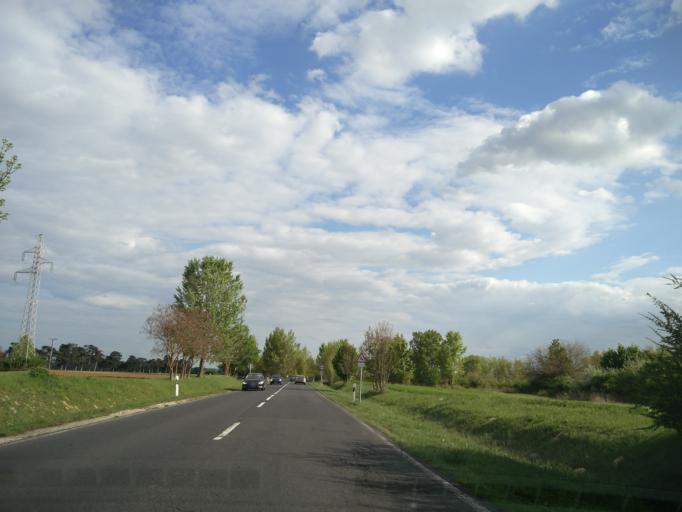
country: HU
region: Zala
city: Keszthely
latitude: 46.7253
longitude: 17.2306
